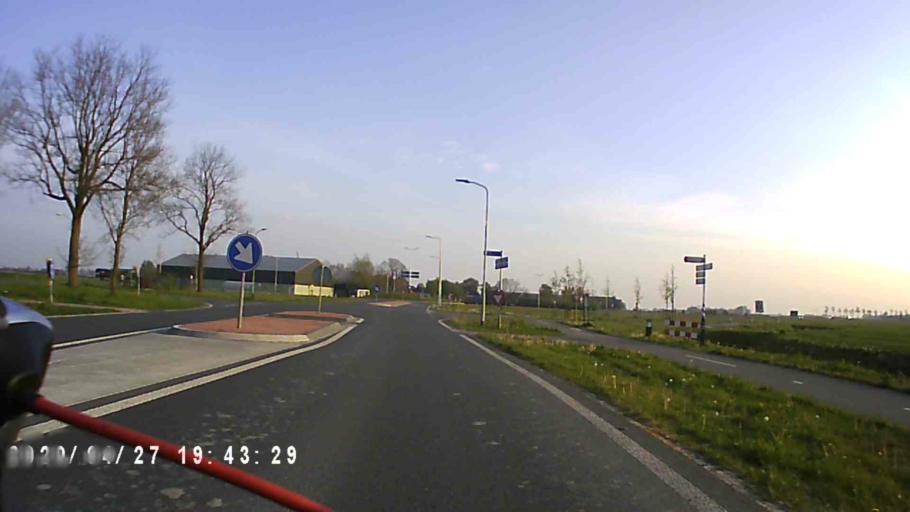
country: NL
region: Groningen
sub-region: Gemeente Winsum
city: Winsum
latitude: 53.3549
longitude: 6.4654
